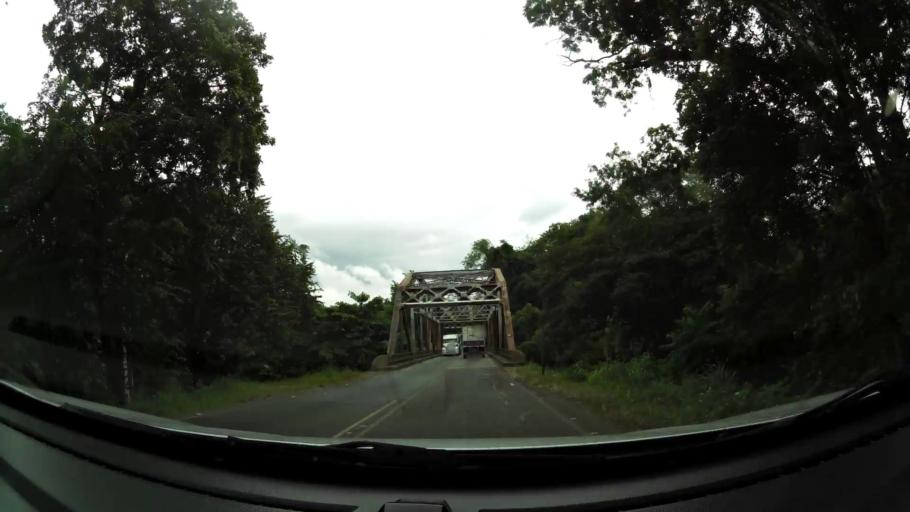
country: CR
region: Guanacaste
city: Juntas
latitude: 10.1627
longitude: -84.9183
